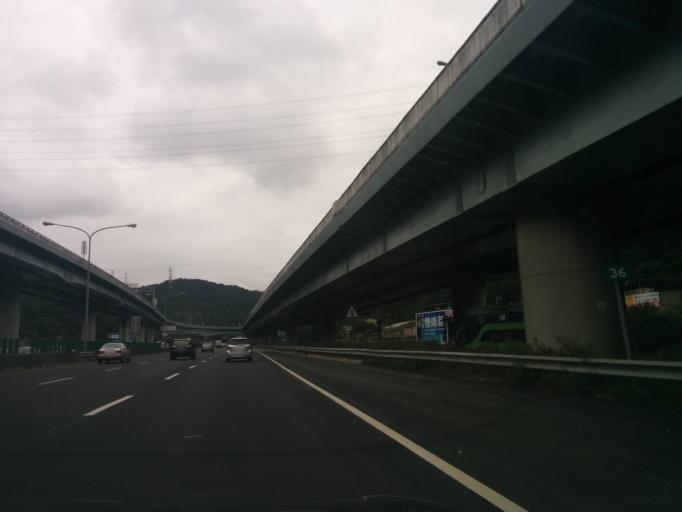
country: TW
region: Taipei
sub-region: Taipei
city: Banqiao
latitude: 25.0592
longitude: 121.4114
